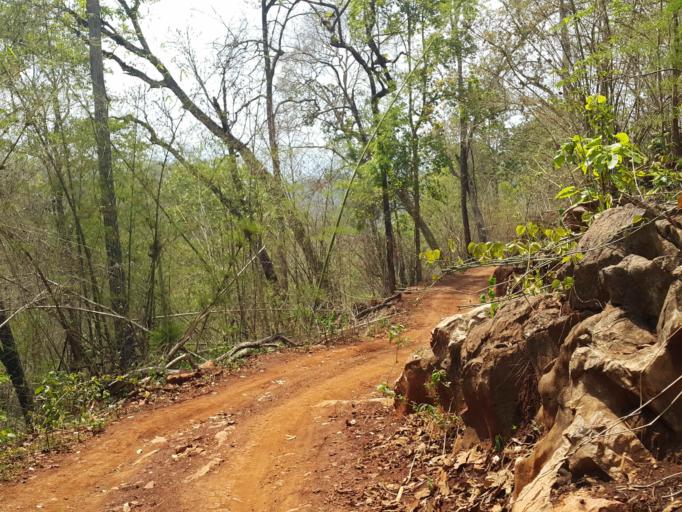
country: TH
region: Chiang Mai
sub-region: Amphoe Chiang Dao
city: Chiang Dao
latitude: 19.3069
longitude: 98.7254
